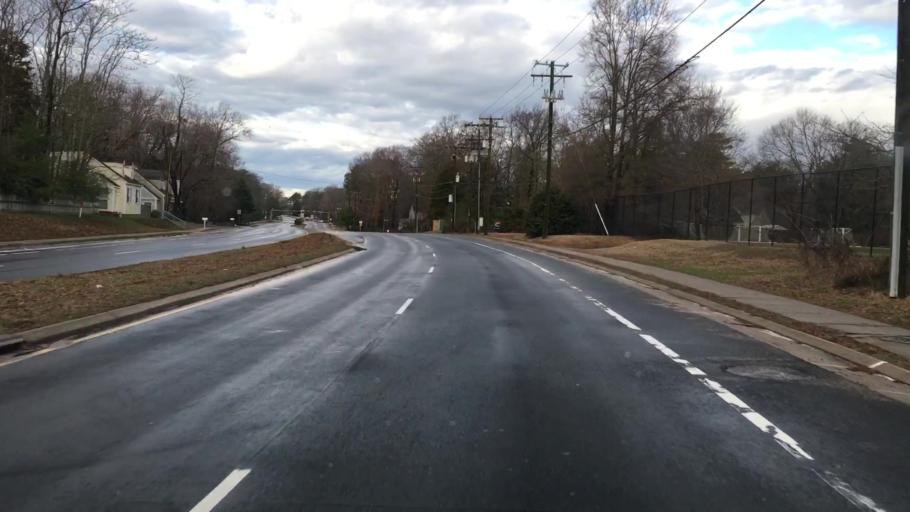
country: US
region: Virginia
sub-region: Chesterfield County
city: Bon Air
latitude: 37.5156
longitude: -77.5928
